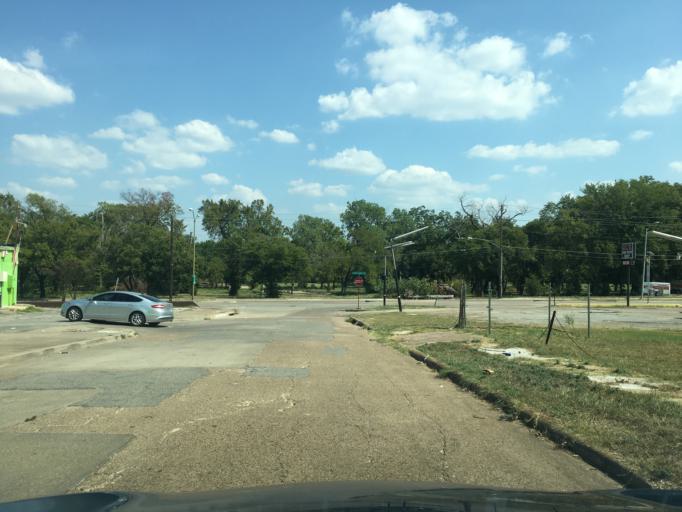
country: US
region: Texas
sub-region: Dallas County
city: Dallas
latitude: 32.7406
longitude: -96.7896
